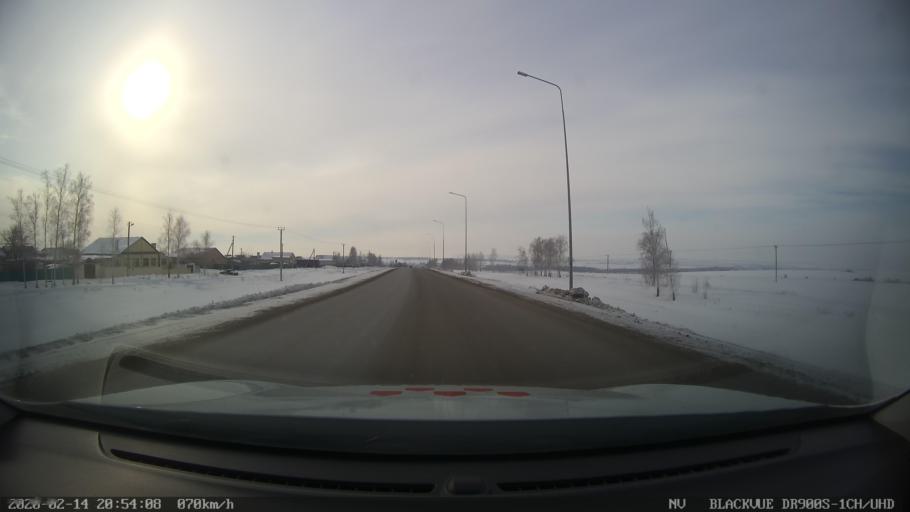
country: RU
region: Tatarstan
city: Kuybyshevskiy Zaton
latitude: 55.1887
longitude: 49.2453
